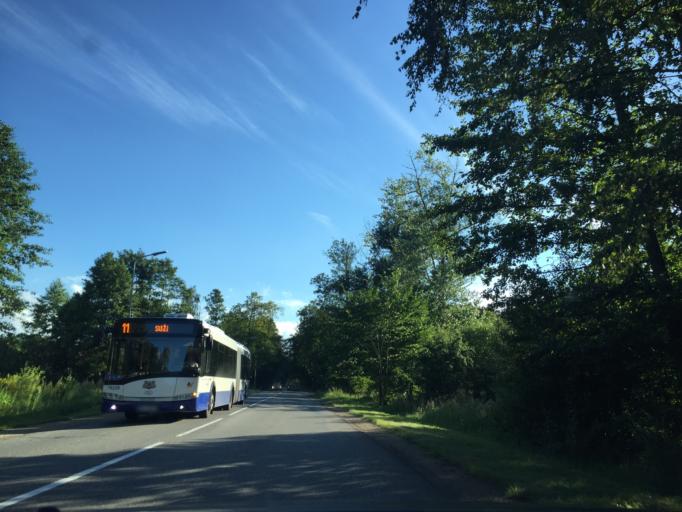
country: LV
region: Riga
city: Jaunciems
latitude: 57.0519
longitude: 24.1285
